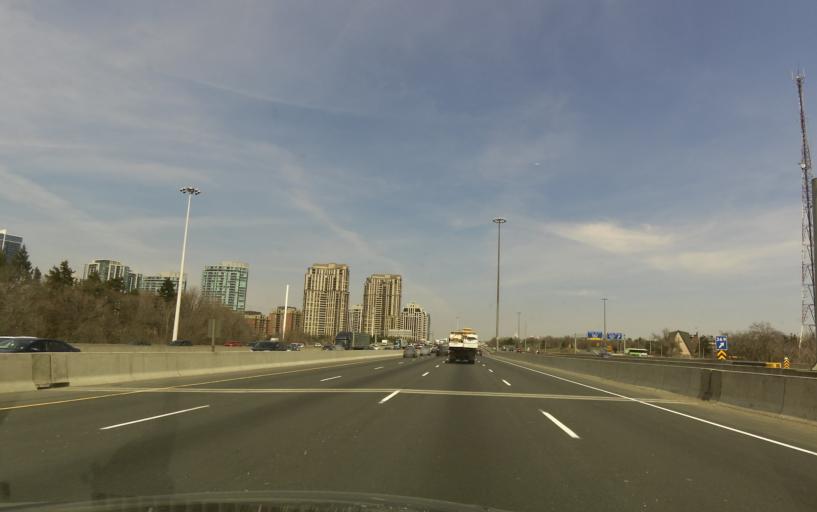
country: CA
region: Ontario
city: North York
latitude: 43.7517
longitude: -79.4111
